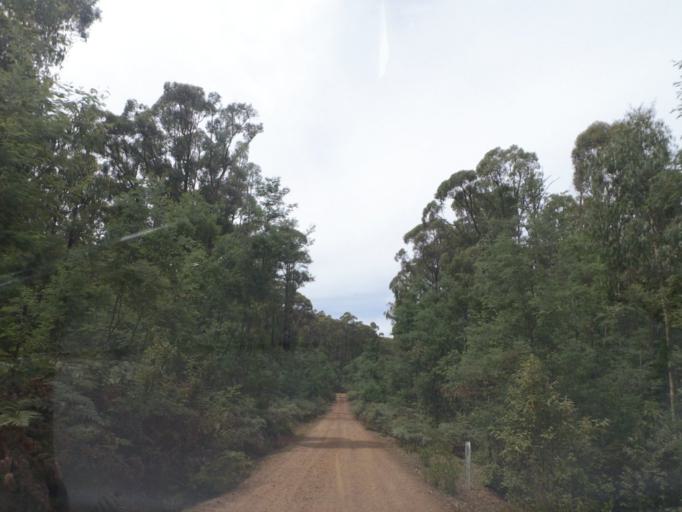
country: AU
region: Victoria
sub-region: Yarra Ranges
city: Healesville
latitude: -37.4437
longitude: 145.5841
